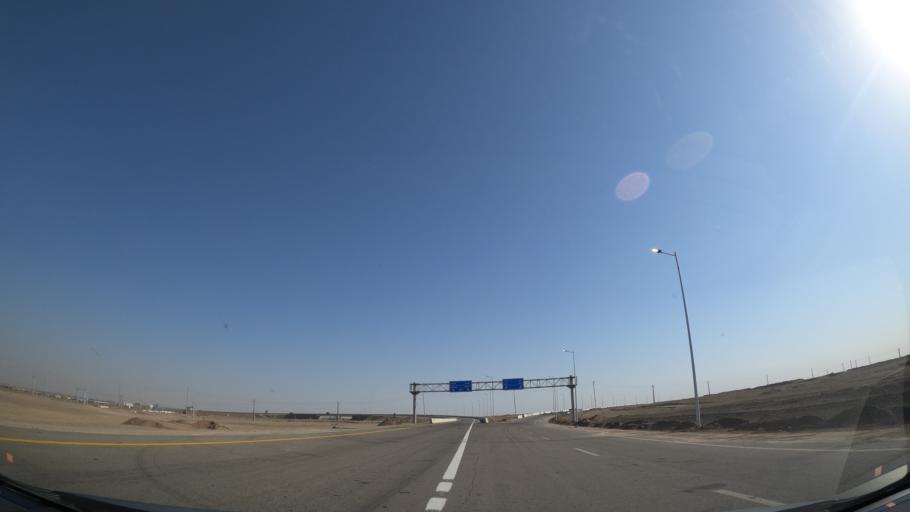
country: IR
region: Tehran
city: Eqbaliyeh
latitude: 35.1363
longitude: 51.5073
